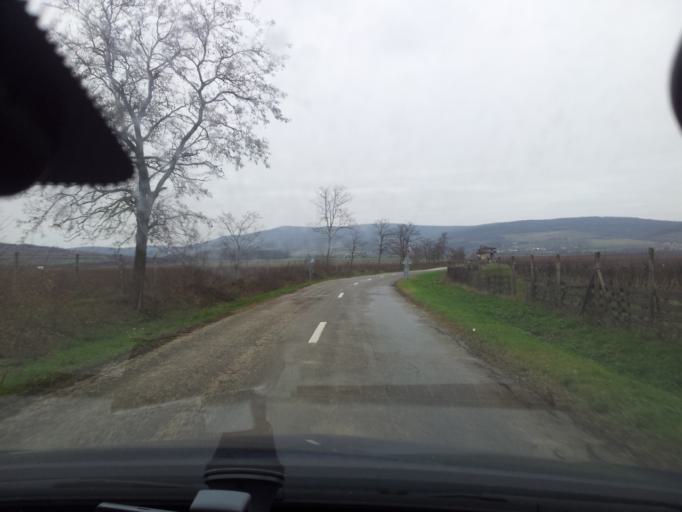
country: HU
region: Borsod-Abauj-Zemplen
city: Satoraljaujhely
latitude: 48.4466
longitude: 21.6572
